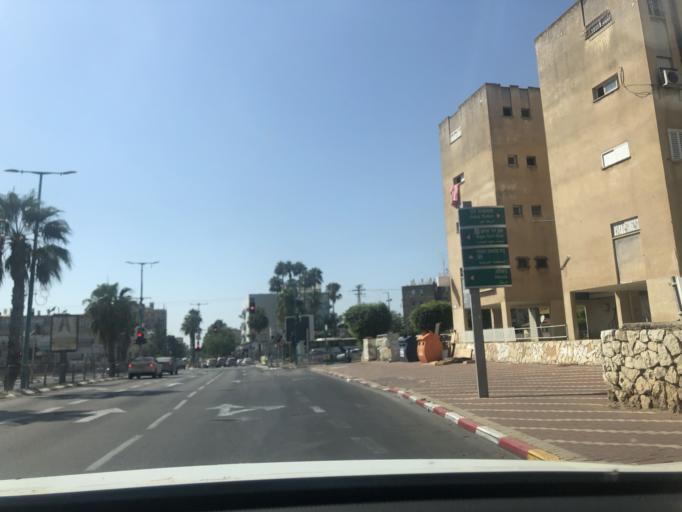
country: IL
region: Central District
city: Lod
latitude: 31.9461
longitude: 34.8929
